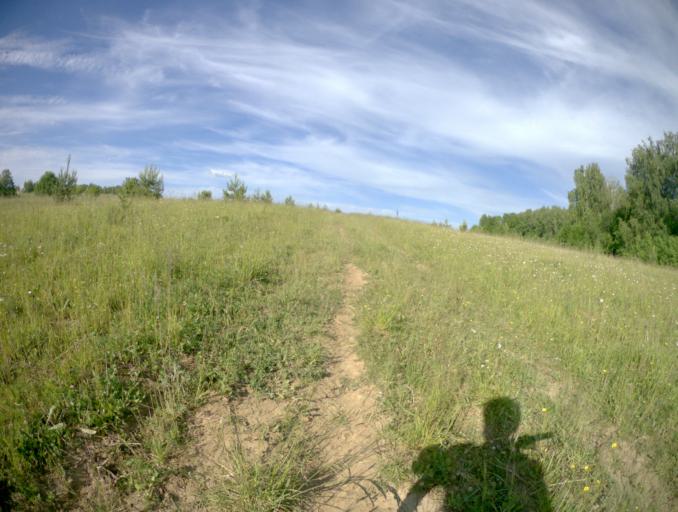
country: RU
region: Vladimir
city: Vorsha
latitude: 56.1750
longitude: 40.1799
